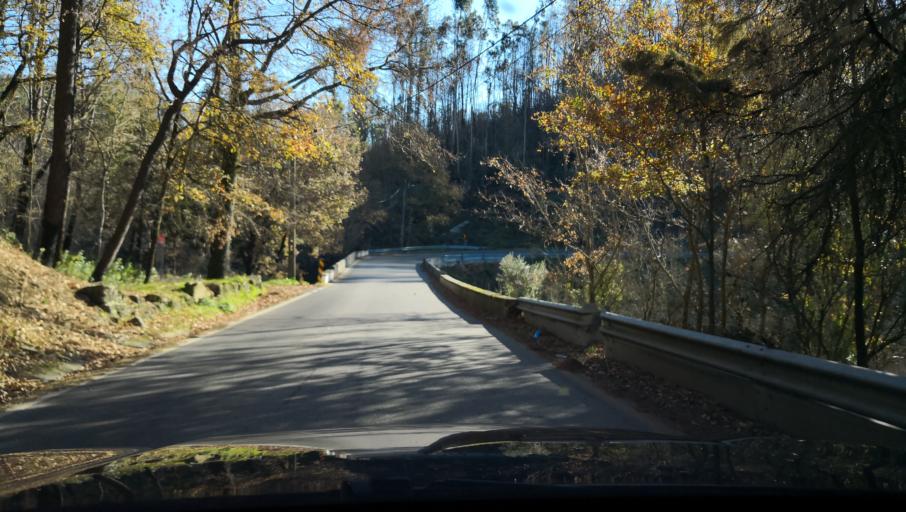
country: PT
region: Viseu
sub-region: Oliveira de Frades
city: Oliveira de Frades
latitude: 40.7295
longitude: -8.1509
